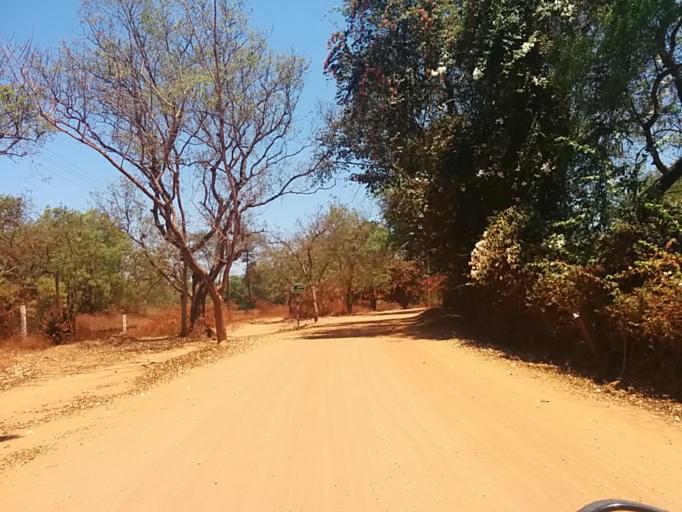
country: IN
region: Tamil Nadu
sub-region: Villupuram
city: Auroville
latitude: 12.0074
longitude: 79.8082
